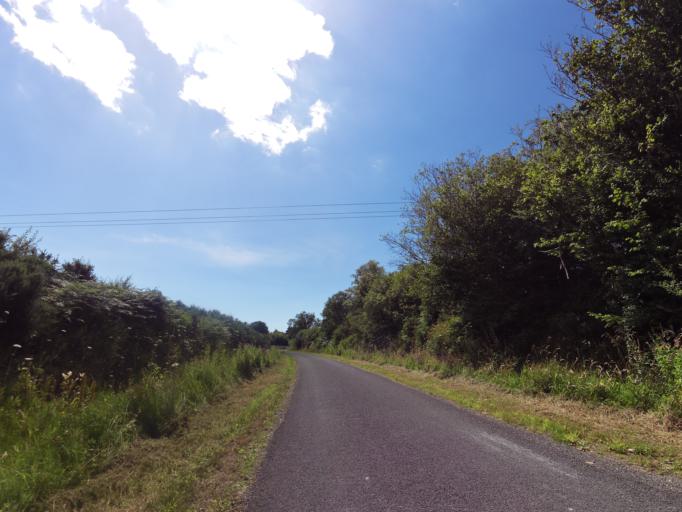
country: IE
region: Munster
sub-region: Waterford
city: Portlaw
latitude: 52.2368
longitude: -7.3002
